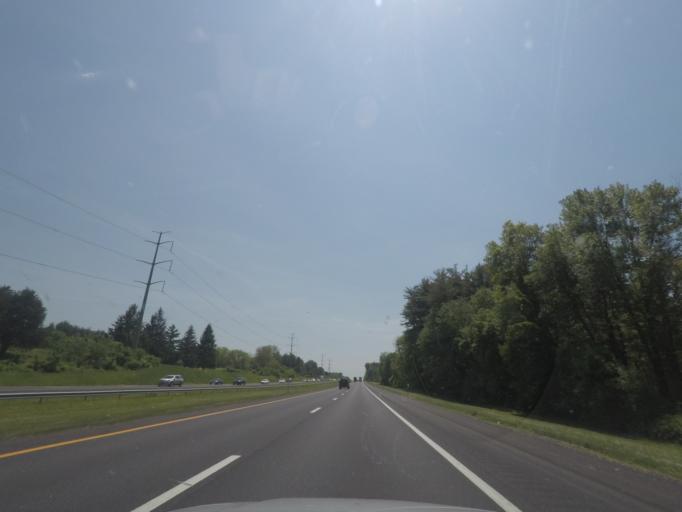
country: US
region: New York
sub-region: Ulster County
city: Hurley
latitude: 41.9148
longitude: -74.0440
